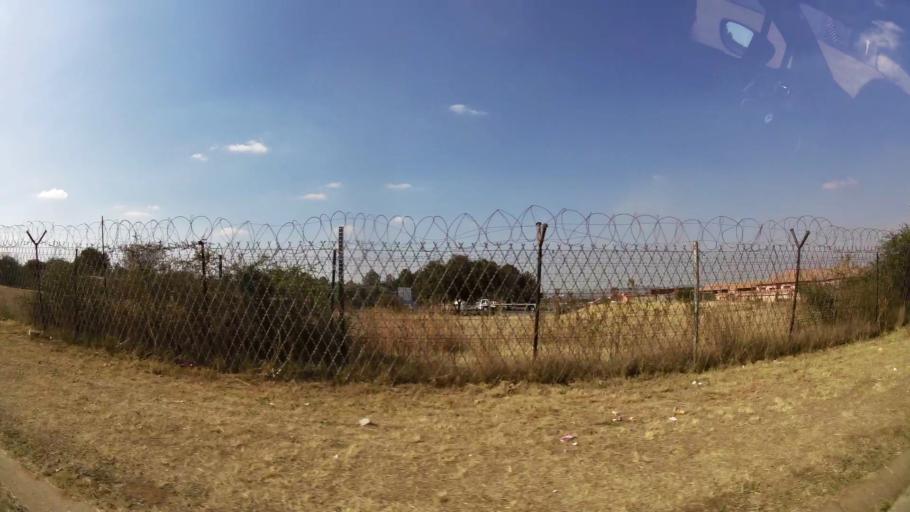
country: ZA
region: Gauteng
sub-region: City of Johannesburg Metropolitan Municipality
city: Roodepoort
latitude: -26.1652
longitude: 27.8014
